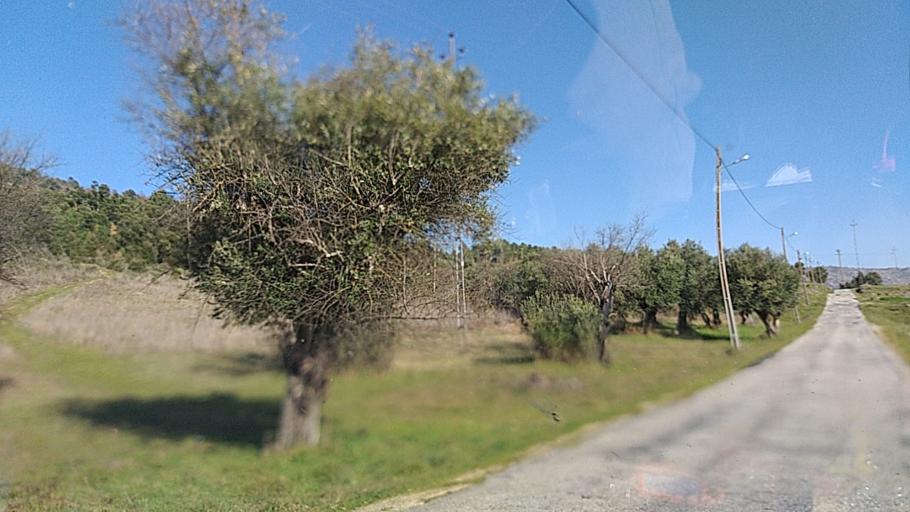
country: PT
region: Guarda
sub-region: Celorico da Beira
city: Celorico da Beira
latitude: 40.6885
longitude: -7.4544
